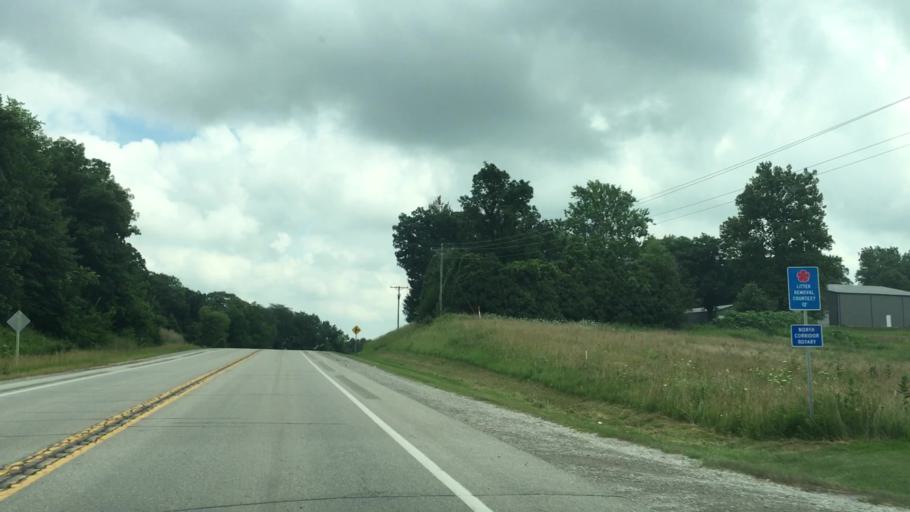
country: US
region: Iowa
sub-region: Johnson County
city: Tiffin
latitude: 41.7114
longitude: -91.6947
